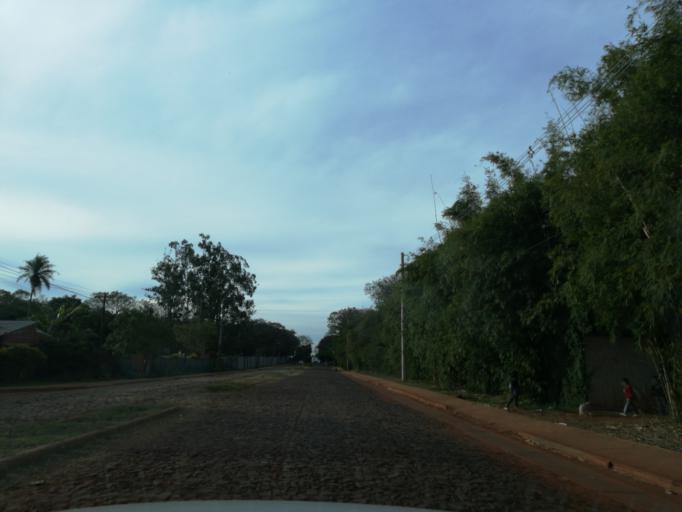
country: AR
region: Misiones
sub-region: Departamento de Capital
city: Posadas
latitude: -27.3570
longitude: -55.9265
